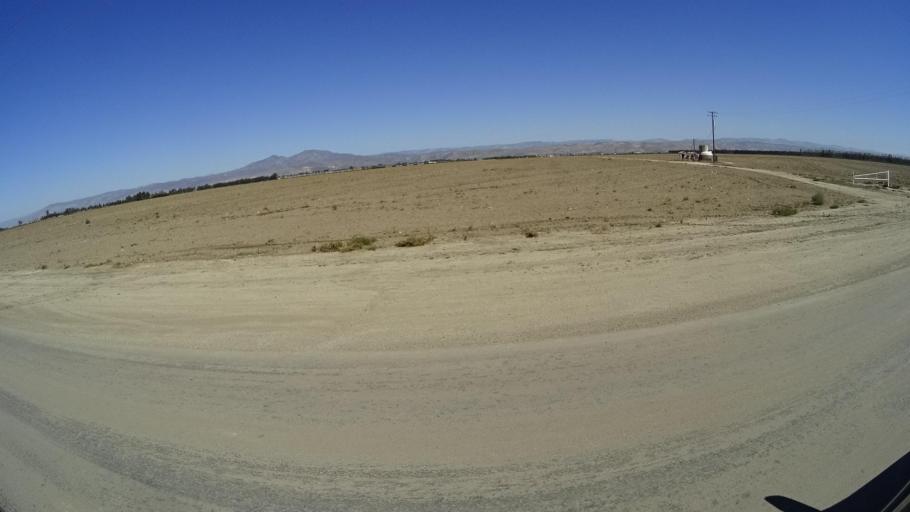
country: US
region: California
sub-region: Monterey County
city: Greenfield
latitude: 36.2966
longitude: -121.2619
